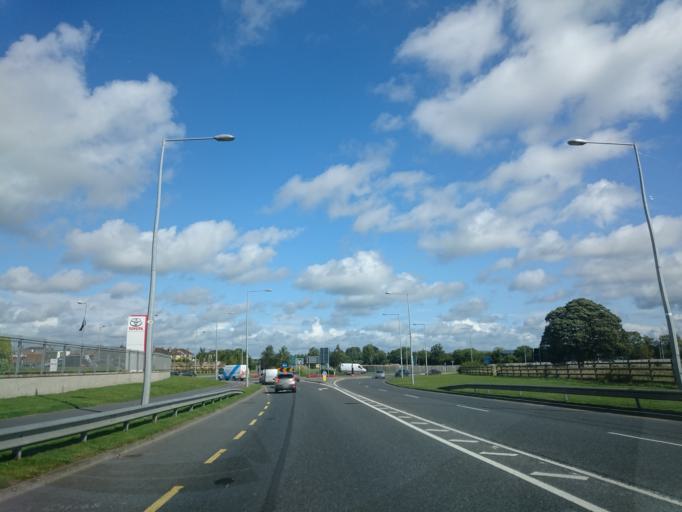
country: IE
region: Leinster
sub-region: Kilkenny
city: Kilkenny
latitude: 52.6574
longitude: -7.2256
